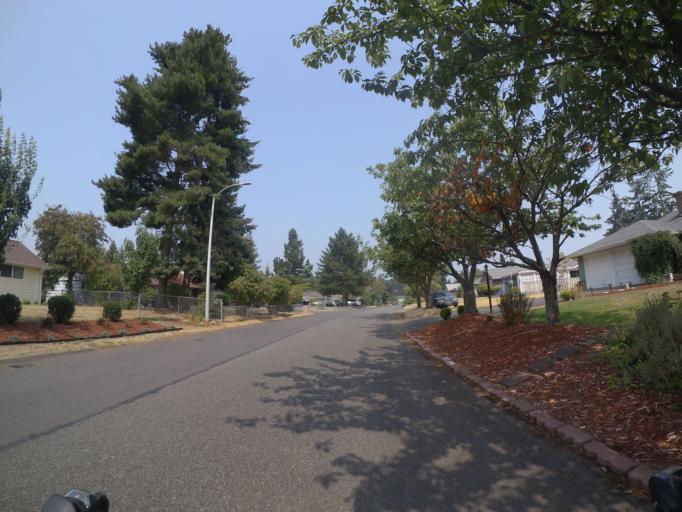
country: US
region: Washington
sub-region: Pierce County
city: Lakewood
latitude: 47.1605
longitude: -122.5092
